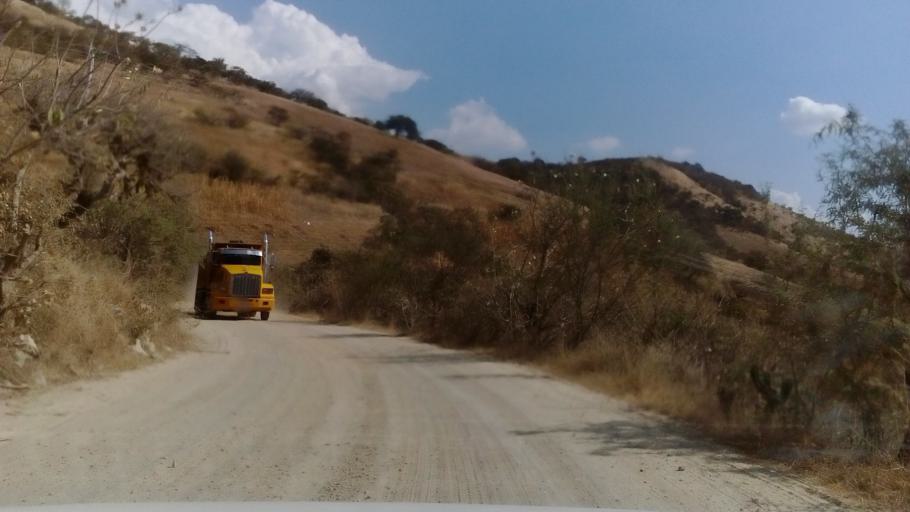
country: MX
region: Guanajuato
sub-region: Silao de la Victoria
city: Loma de Yerbabuena
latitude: 21.0711
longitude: -101.4569
